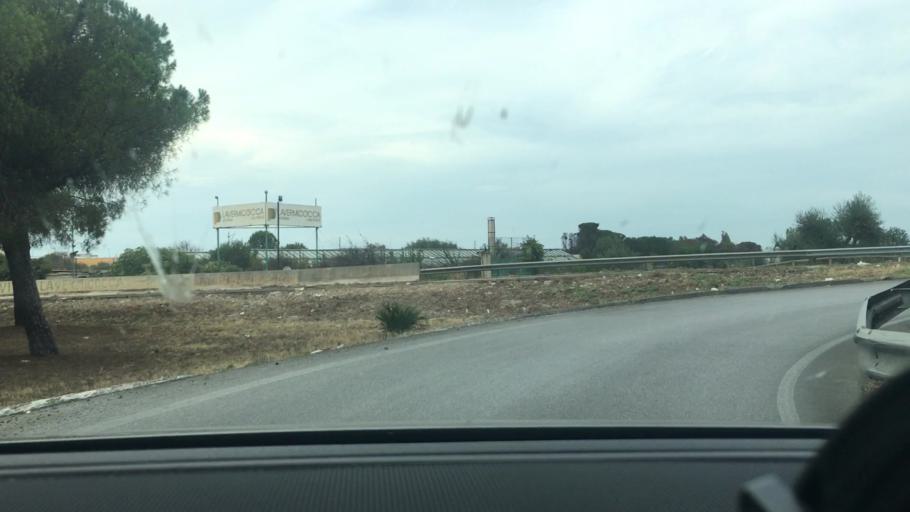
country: IT
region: Apulia
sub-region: Provincia di Bari
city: Bari
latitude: 41.0942
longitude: 16.8386
